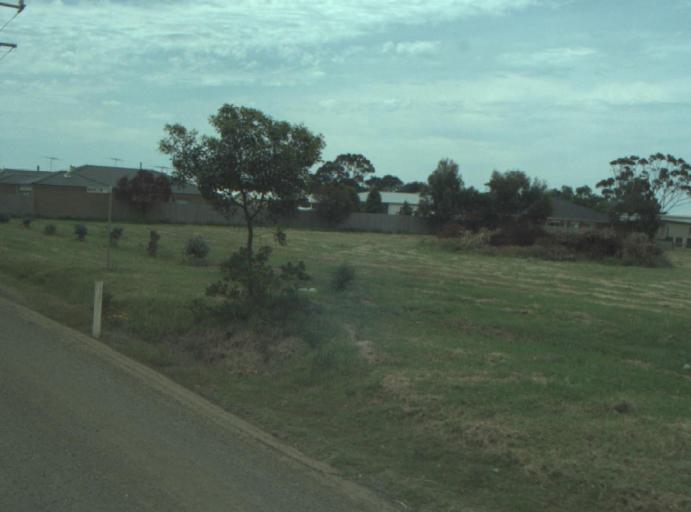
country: AU
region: Victoria
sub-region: Queenscliffe
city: Queenscliff
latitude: -38.1415
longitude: 144.7076
